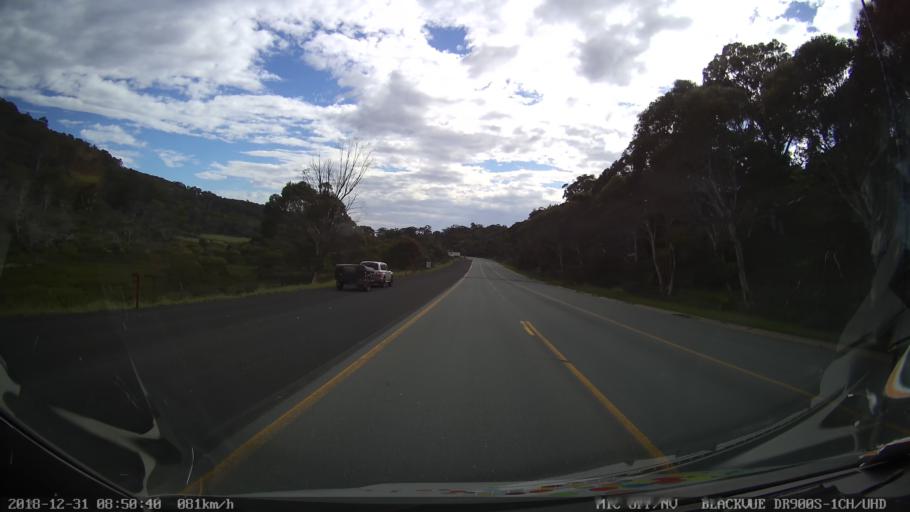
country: AU
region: New South Wales
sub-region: Snowy River
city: Jindabyne
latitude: -36.3514
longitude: 148.5188
